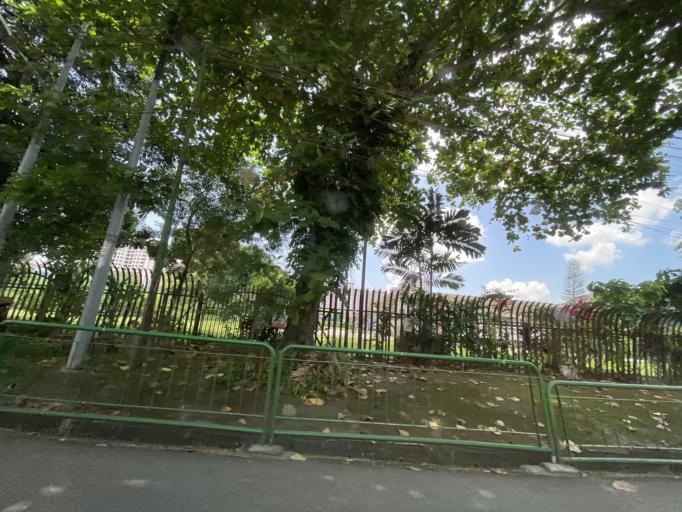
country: MY
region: Johor
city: Kampung Pasir Gudang Baru
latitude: 1.3833
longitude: 103.8782
